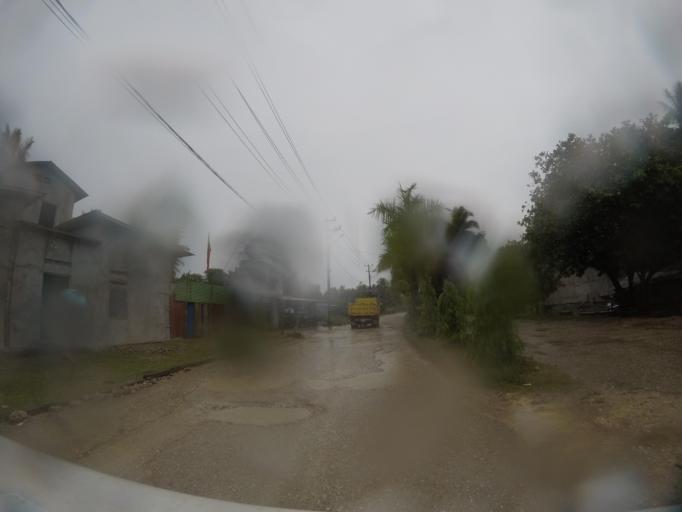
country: TL
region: Lautem
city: Lospalos
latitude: -8.5147
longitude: 127.0020
